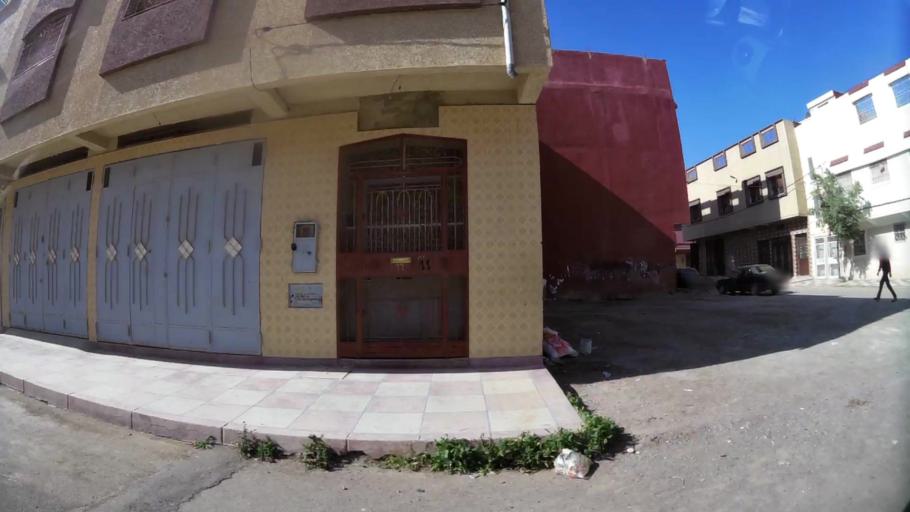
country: MA
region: Oriental
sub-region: Oujda-Angad
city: Oujda
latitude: 34.6832
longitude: -1.9355
